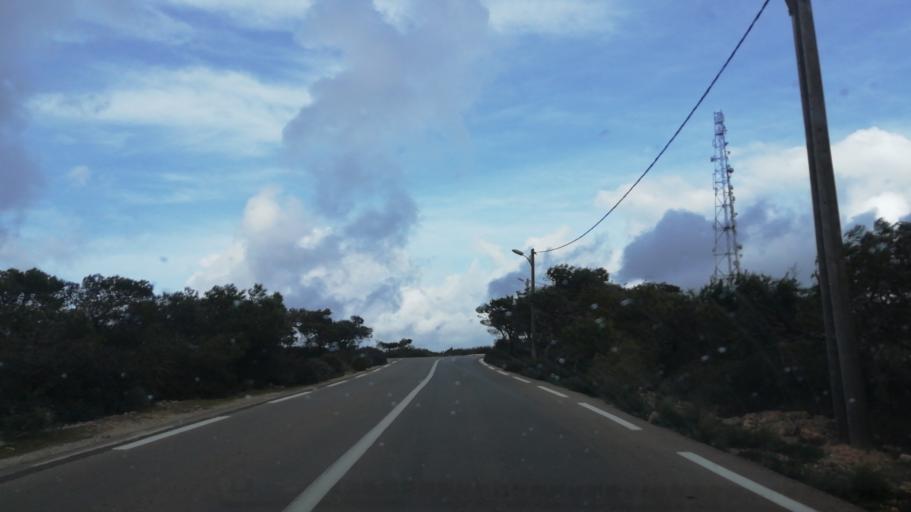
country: DZ
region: Oran
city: Oran
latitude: 35.7028
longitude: -0.6765
